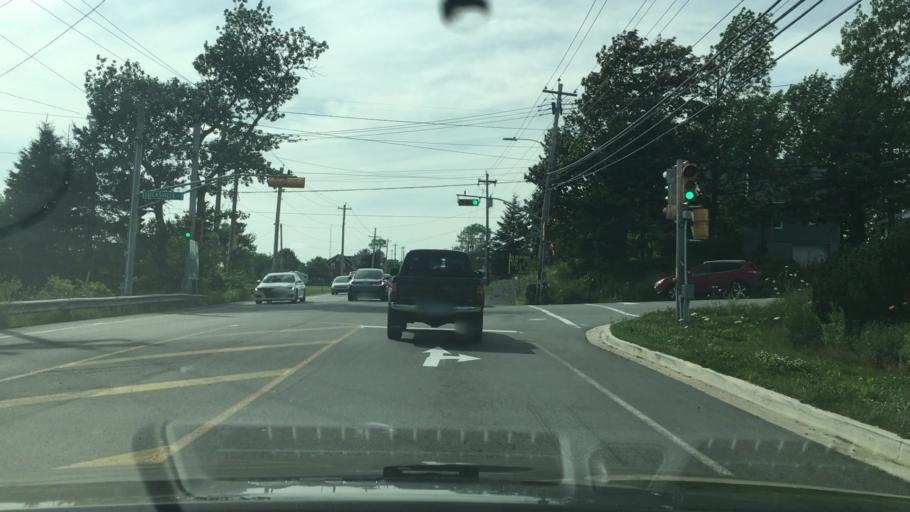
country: CA
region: Nova Scotia
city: Dartmouth
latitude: 44.7322
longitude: -63.7589
